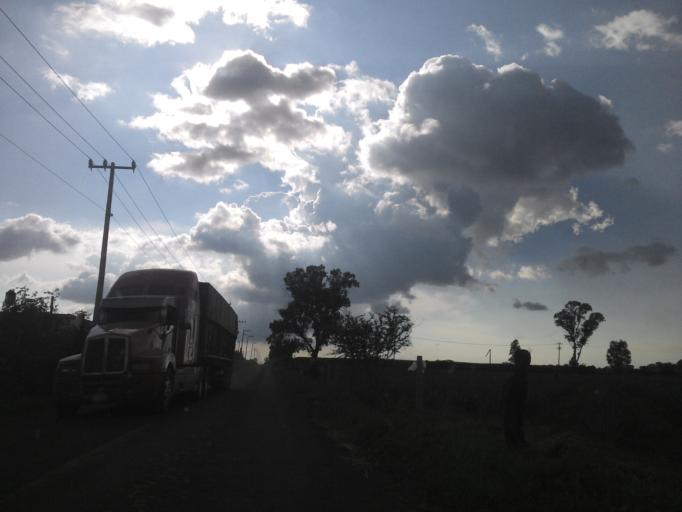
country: MX
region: Jalisco
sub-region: Atotonilco el Alto
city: Ojo de Agua de Moran
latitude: 20.6032
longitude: -102.4717
